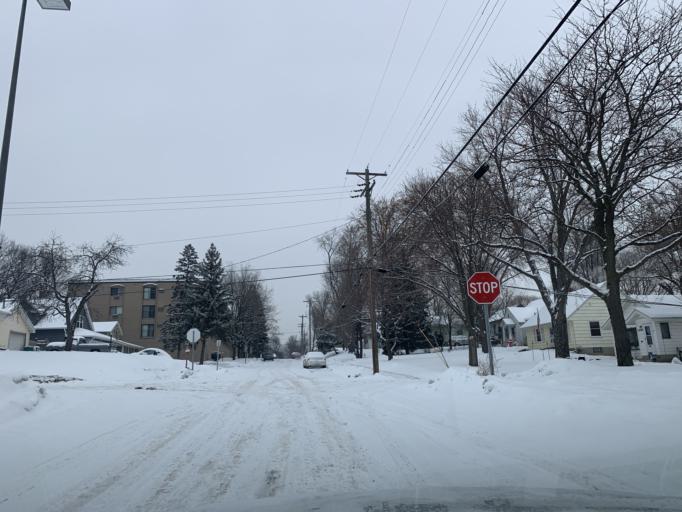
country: US
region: Minnesota
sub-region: Hennepin County
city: Saint Louis Park
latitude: 44.9466
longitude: -93.3391
